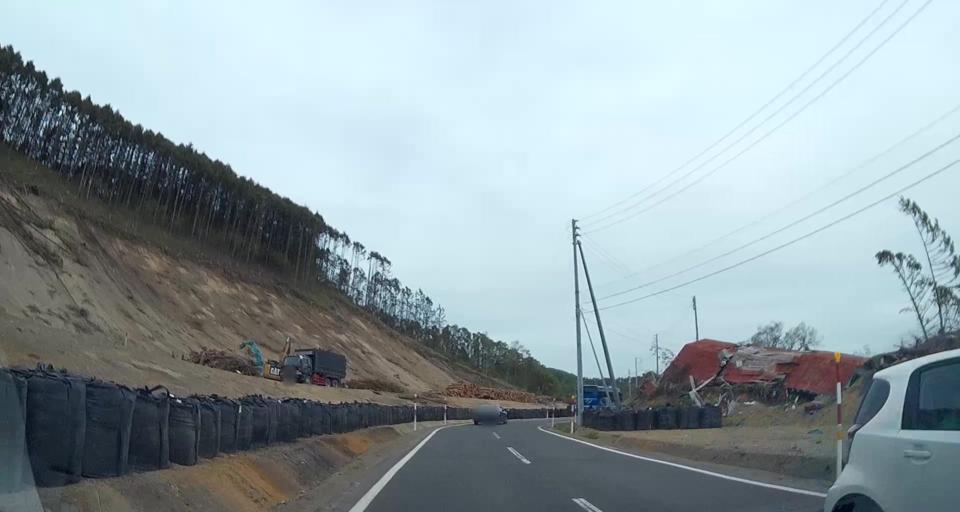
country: JP
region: Hokkaido
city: Chitose
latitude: 42.7520
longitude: 141.9143
